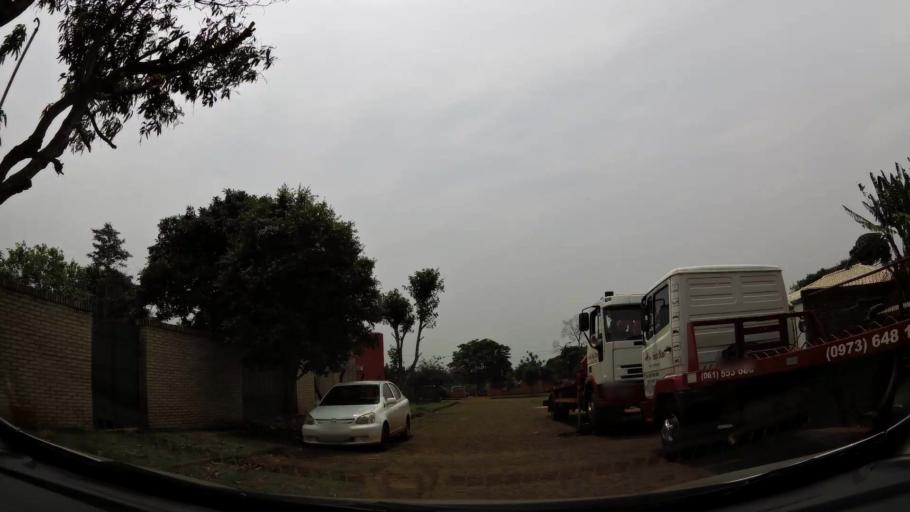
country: PY
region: Alto Parana
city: Presidente Franco
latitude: -25.5549
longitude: -54.6239
